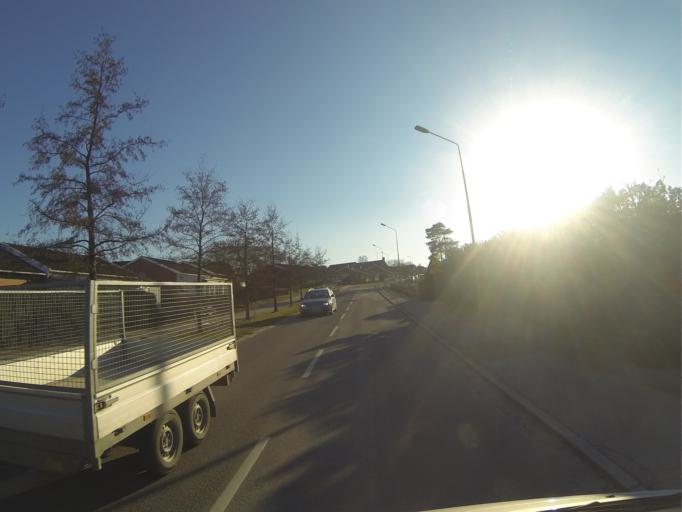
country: SE
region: Skane
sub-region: Hoors Kommun
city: Loberod
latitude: 55.7777
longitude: 13.5177
